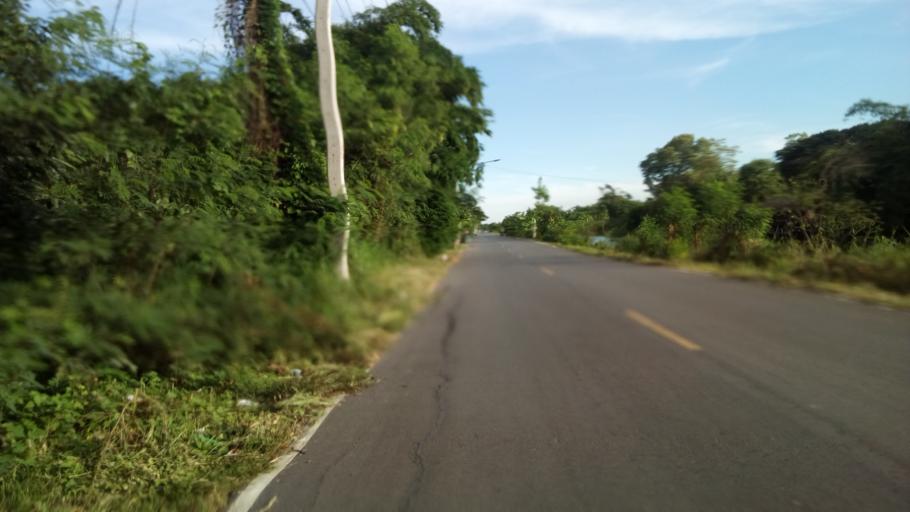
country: TH
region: Pathum Thani
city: Nong Suea
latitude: 14.0589
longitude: 100.8469
